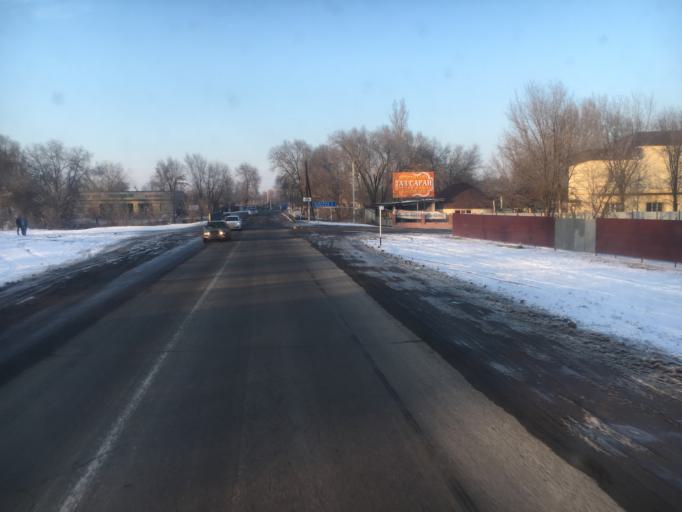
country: KZ
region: Almaty Oblysy
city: Burunday
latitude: 43.3655
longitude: 76.6417
